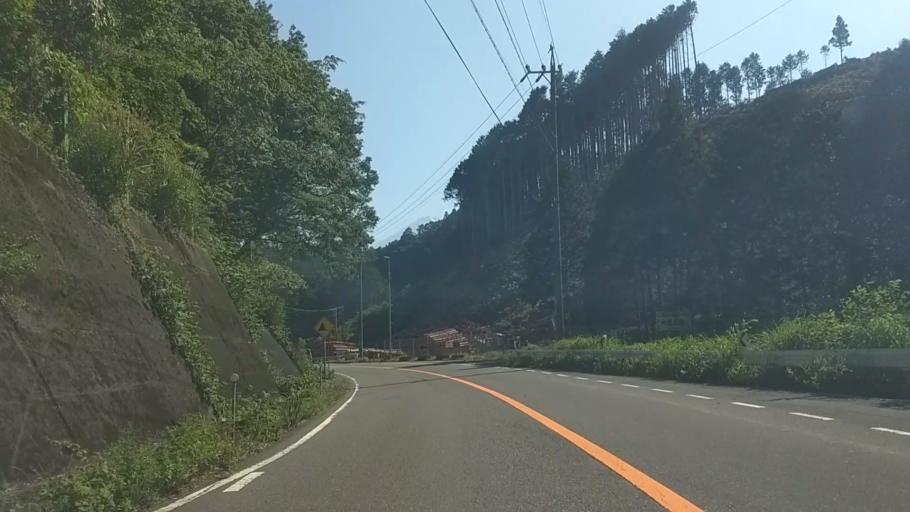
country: JP
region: Shizuoka
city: Fujinomiya
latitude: 35.1834
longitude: 138.5276
